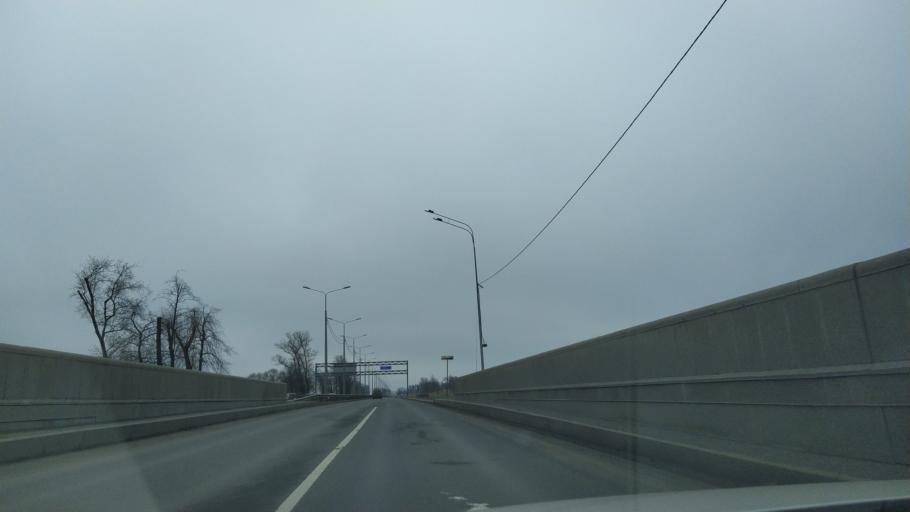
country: RU
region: St.-Petersburg
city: Aleksandrovskaya
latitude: 59.7762
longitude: 30.3285
